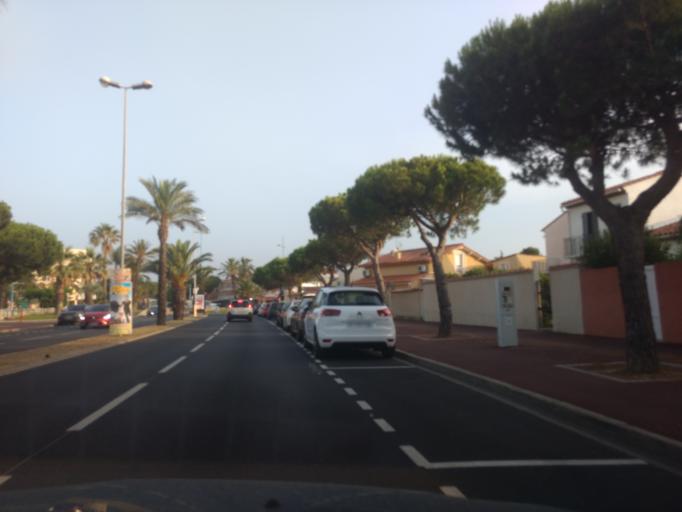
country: FR
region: Languedoc-Roussillon
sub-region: Departement des Pyrenees-Orientales
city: Saint-Cyprien-Plage
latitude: 42.6299
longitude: 3.0320
